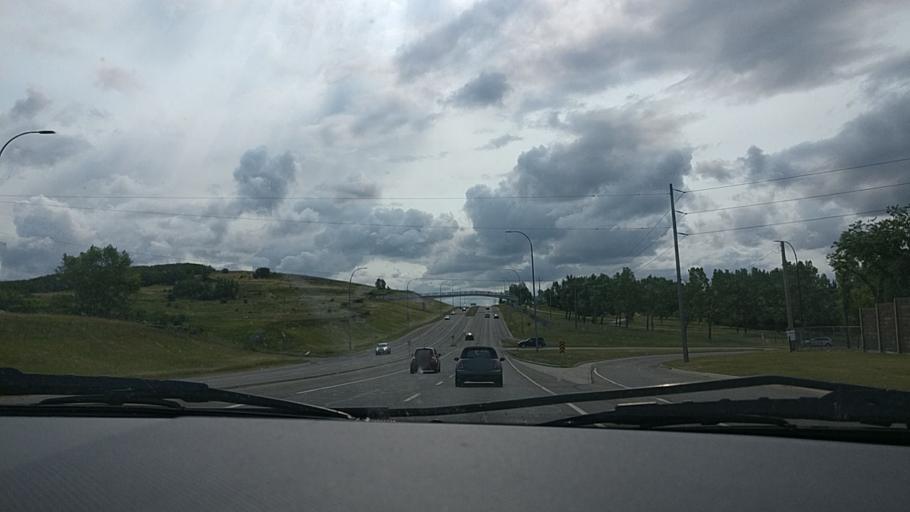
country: CA
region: Alberta
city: Calgary
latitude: 51.1037
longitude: -114.1285
